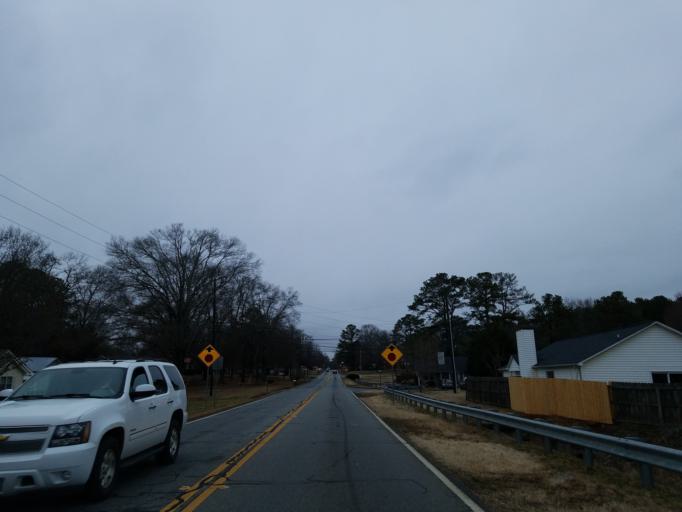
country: US
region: Georgia
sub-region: Bartow County
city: Cartersville
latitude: 34.2009
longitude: -84.8276
